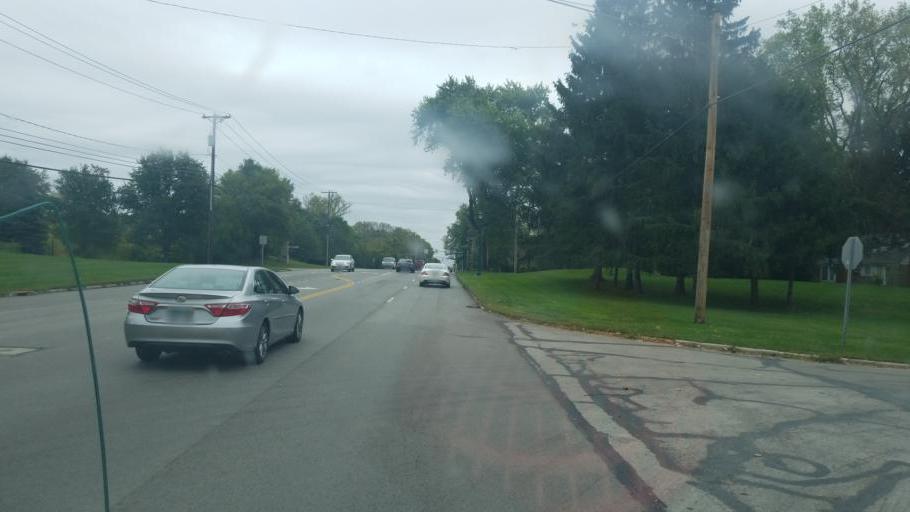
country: US
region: Ohio
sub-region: Lucas County
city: Ottawa Hills
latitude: 41.6769
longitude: -83.6573
